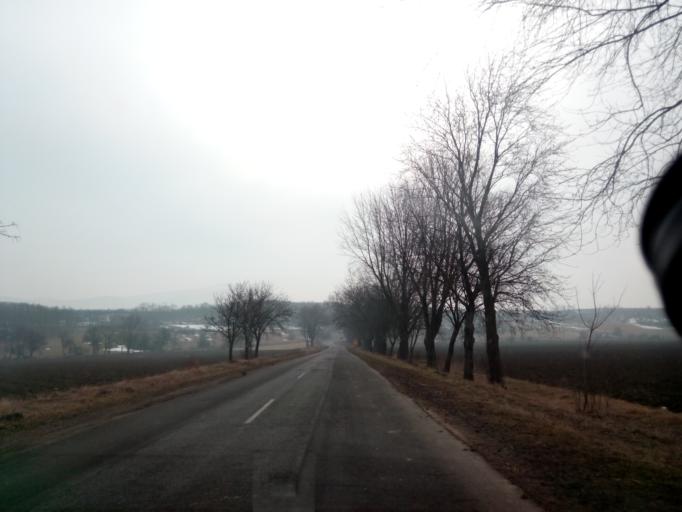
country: HU
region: Borsod-Abauj-Zemplen
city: Gonc
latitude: 48.4832
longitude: 21.2546
